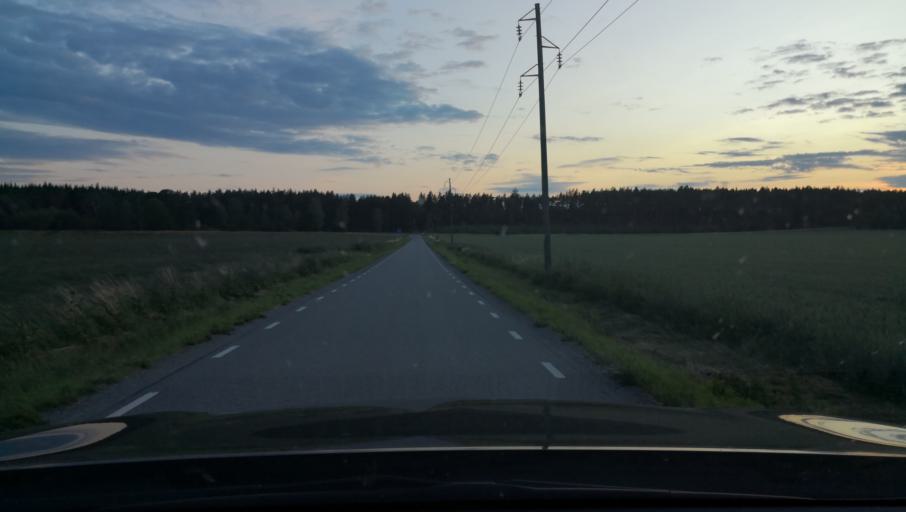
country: SE
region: Uppsala
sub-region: Osthammars Kommun
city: Bjorklinge
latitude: 60.0625
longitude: 17.5518
